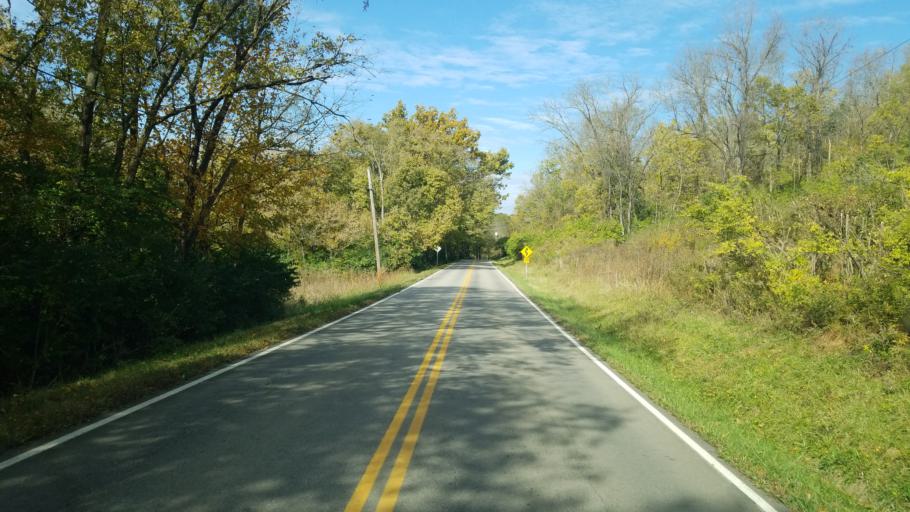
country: US
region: Ohio
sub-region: Warren County
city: Morrow
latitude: 39.3626
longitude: -84.1436
